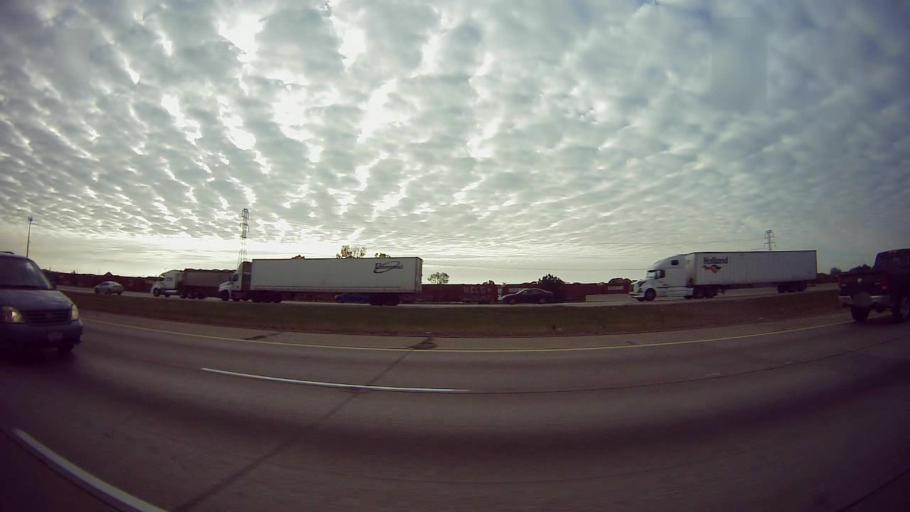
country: US
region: Michigan
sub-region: Wayne County
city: Allen Park
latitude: 42.2680
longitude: -83.2196
